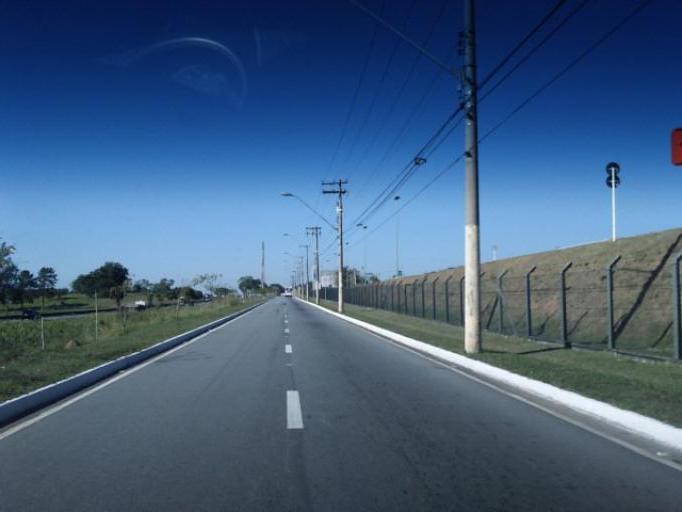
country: BR
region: Sao Paulo
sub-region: Sao Jose Dos Campos
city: Sao Jose dos Campos
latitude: -23.1563
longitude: -45.7928
